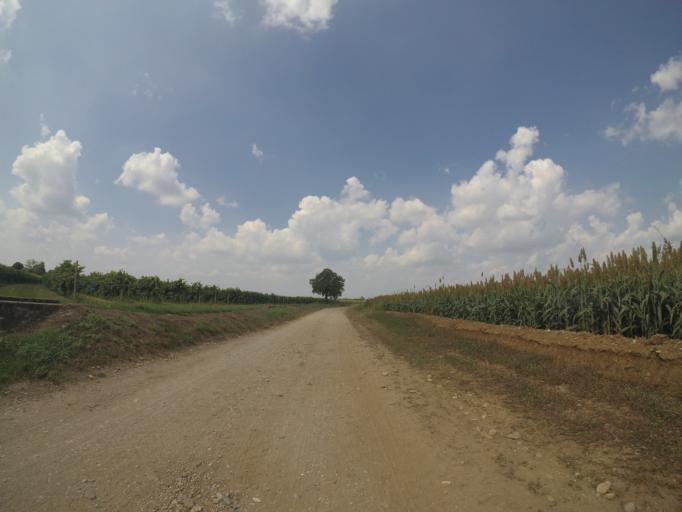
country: IT
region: Friuli Venezia Giulia
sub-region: Provincia di Udine
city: Bertiolo
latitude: 45.9465
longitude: 13.0445
